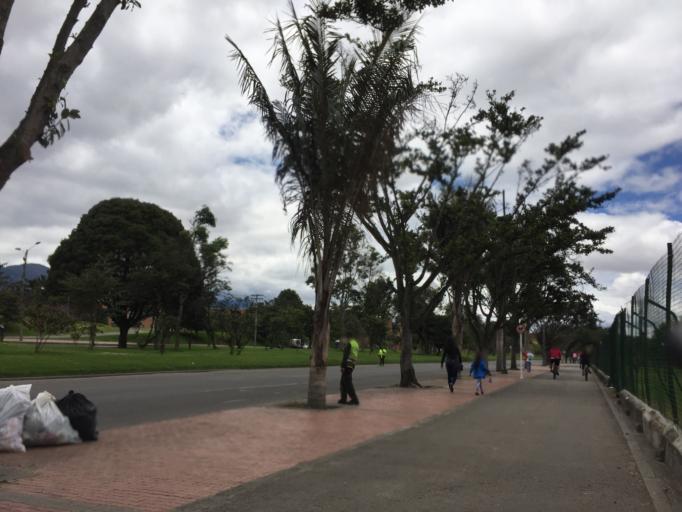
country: CO
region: Bogota D.C.
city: Bogota
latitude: 4.6554
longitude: -74.0908
